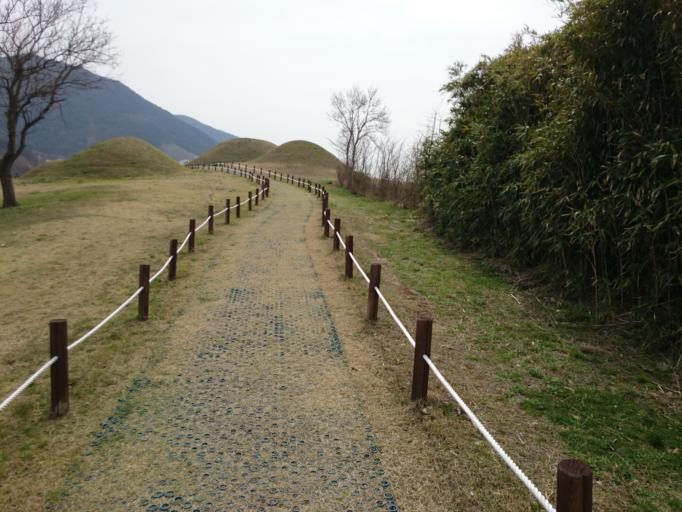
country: KR
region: Gyeongsangnam-do
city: Changnyeong
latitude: 35.5473
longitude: 128.5035
